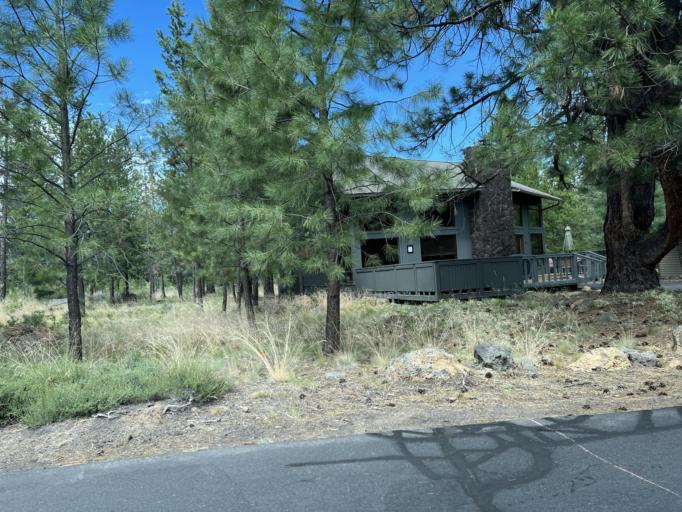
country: US
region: Oregon
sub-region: Deschutes County
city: Sunriver
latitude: 43.8902
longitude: -121.4262
